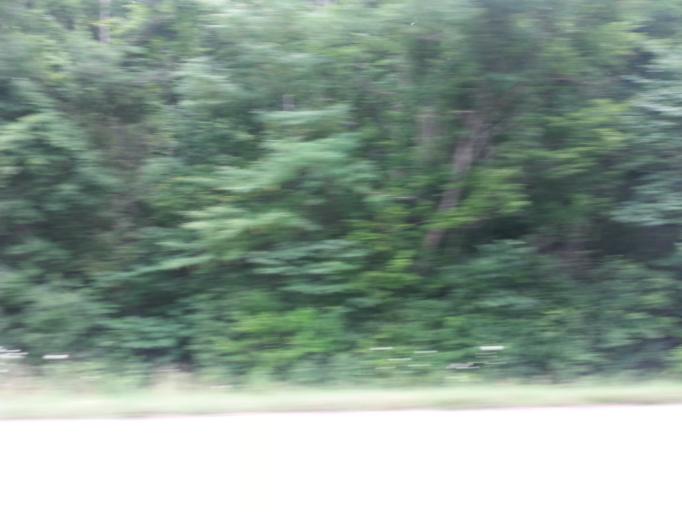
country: US
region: Ohio
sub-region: Brown County
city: Aberdeen
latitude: 38.7020
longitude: -83.7885
